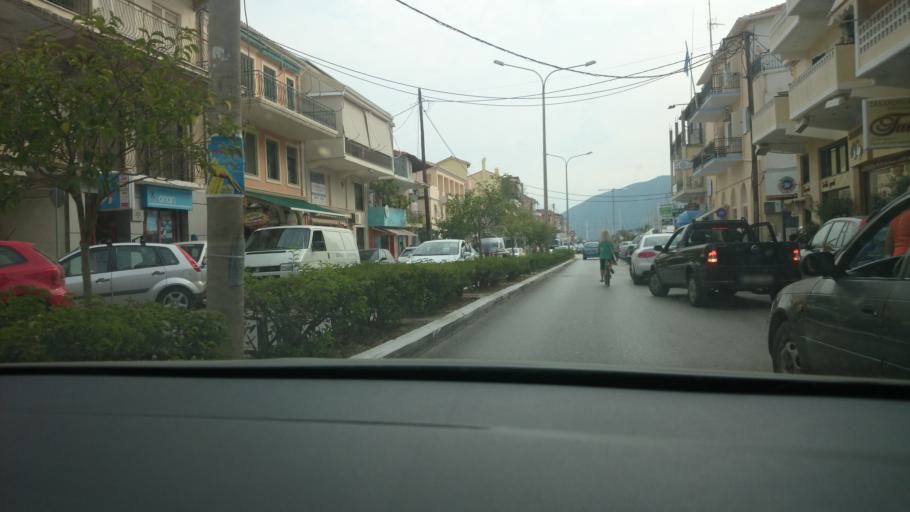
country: GR
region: Ionian Islands
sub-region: Lefkada
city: Lefkada
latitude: 38.8314
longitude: 20.7070
